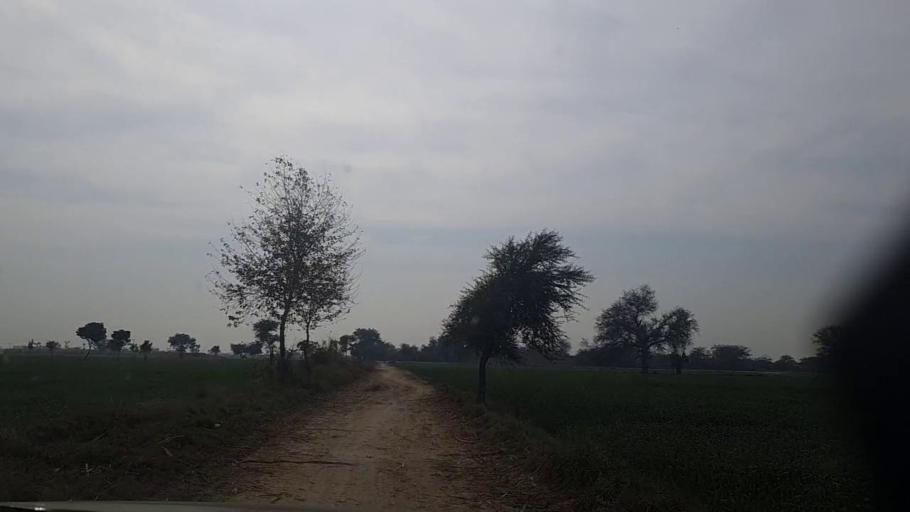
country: PK
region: Sindh
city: Sakrand
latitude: 26.2280
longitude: 68.2970
